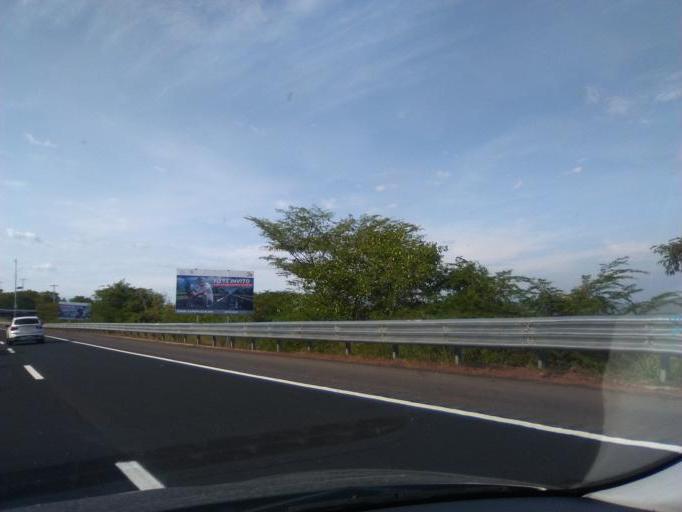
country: MX
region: Morelos
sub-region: Jojutla
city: Higueron
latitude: 18.4767
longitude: -99.1741
